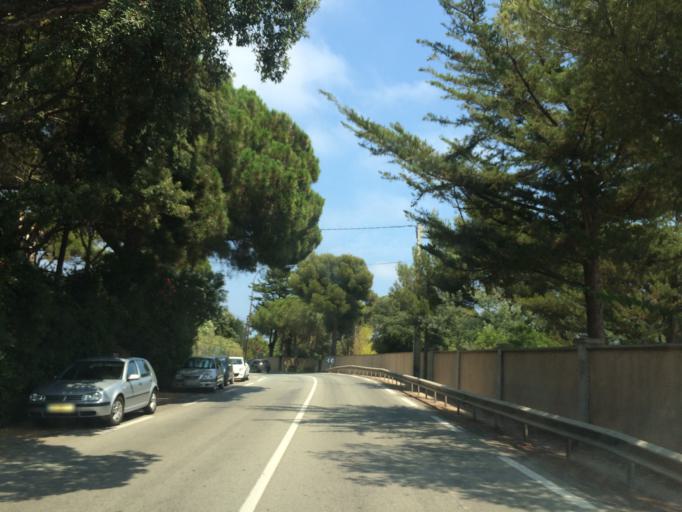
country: FR
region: Provence-Alpes-Cote d'Azur
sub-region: Departement du Var
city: Sainte-Maxime
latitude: 43.3128
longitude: 6.6689
